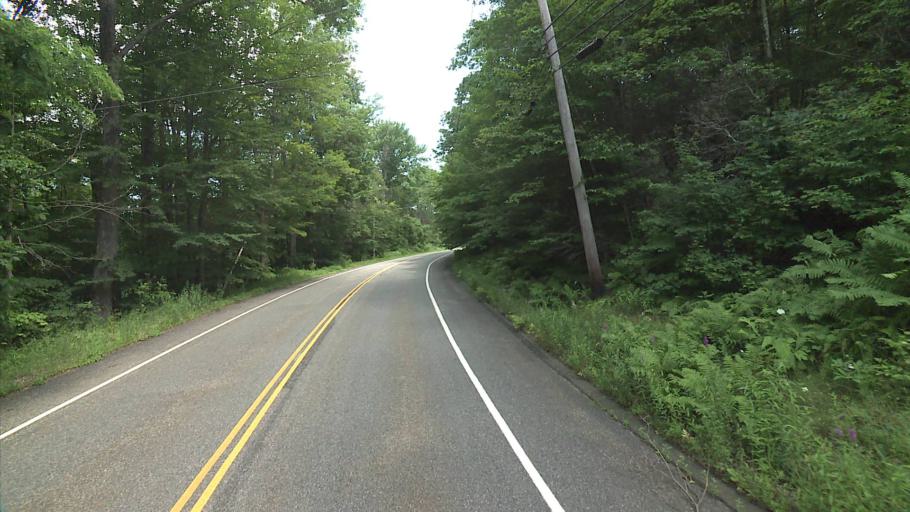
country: US
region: Connecticut
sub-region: Litchfield County
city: Winsted
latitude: 41.9960
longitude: -72.9886
